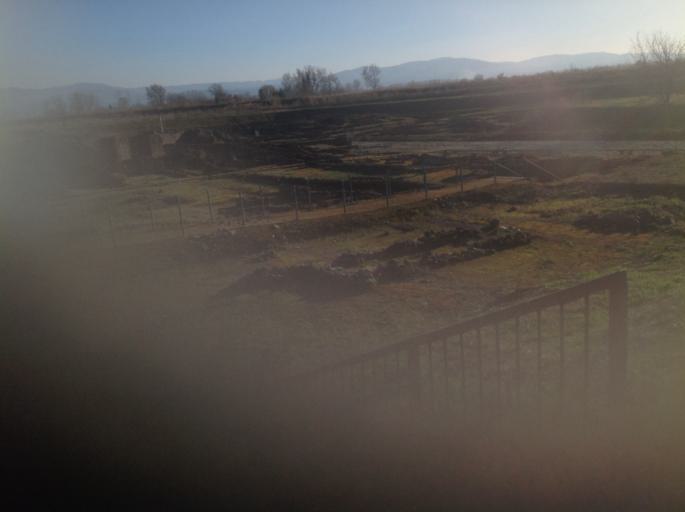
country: IT
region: Calabria
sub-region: Provincia di Cosenza
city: Sibari
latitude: 39.7164
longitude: 16.4910
